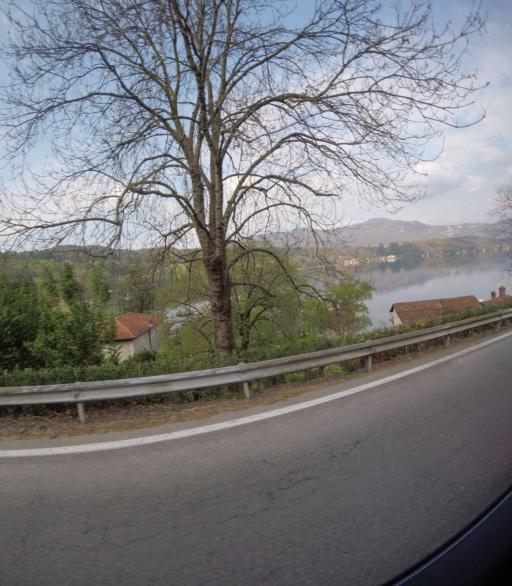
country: IT
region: Piedmont
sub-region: Provincia di Novara
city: Bolzano Novarese
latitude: 45.7660
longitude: 8.4297
